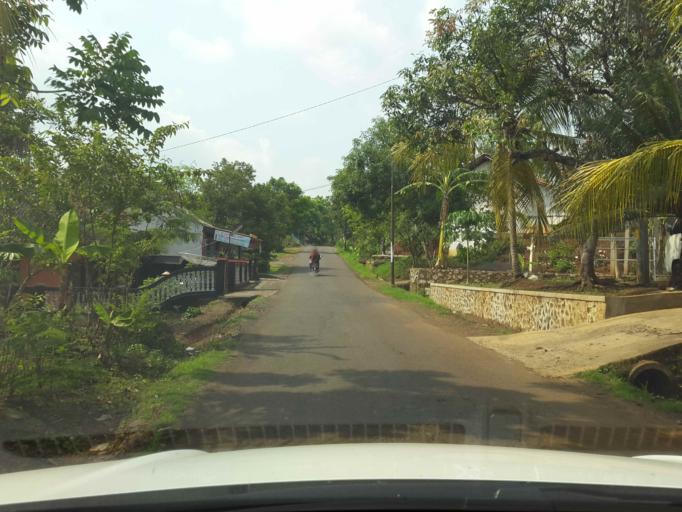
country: ID
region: Central Java
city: Karanganyar
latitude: -7.3231
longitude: 108.6471
